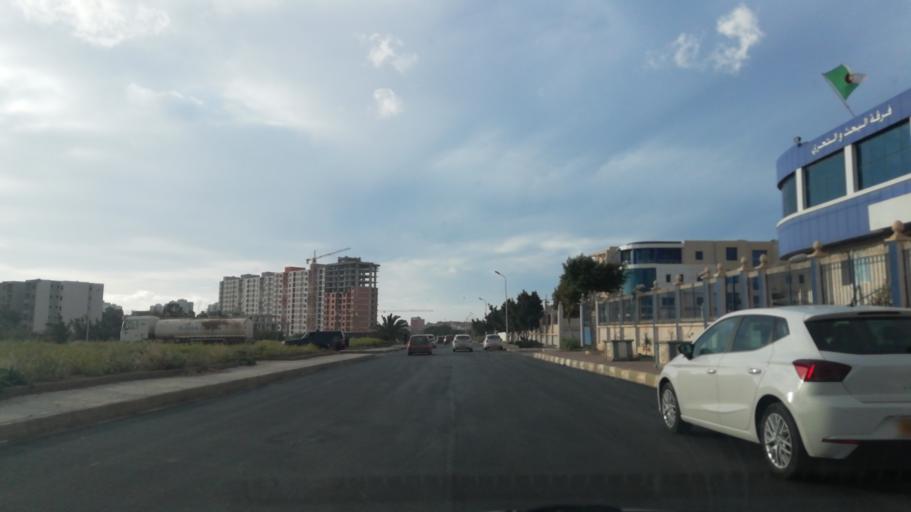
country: DZ
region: Oran
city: Bir el Djir
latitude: 35.7113
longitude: -0.5690
